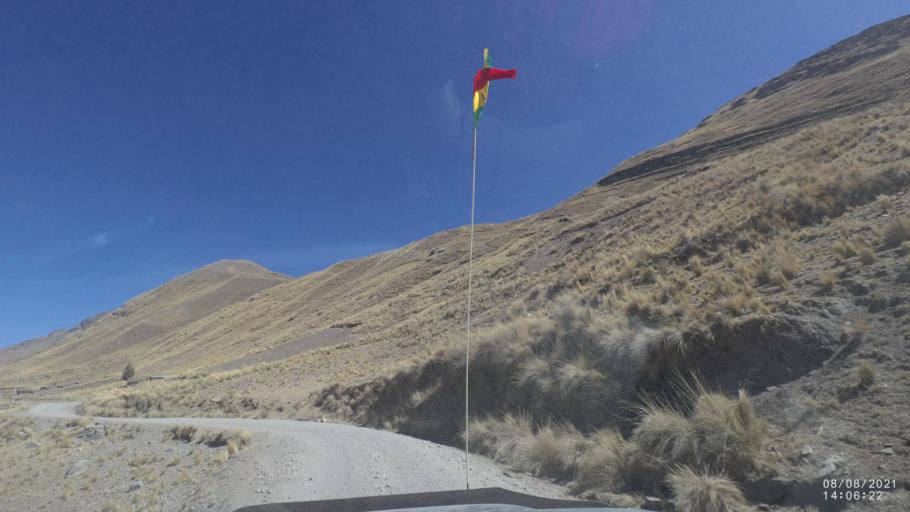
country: BO
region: Cochabamba
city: Sipe Sipe
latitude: -17.1236
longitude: -66.4414
